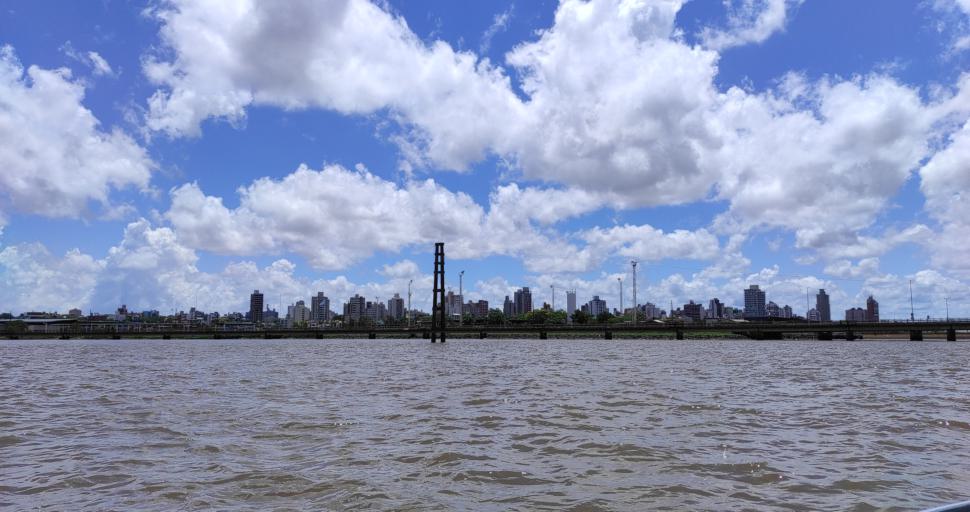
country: AR
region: Misiones
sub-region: Departamento de Capital
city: Posadas
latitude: -27.3779
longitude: -55.8792
